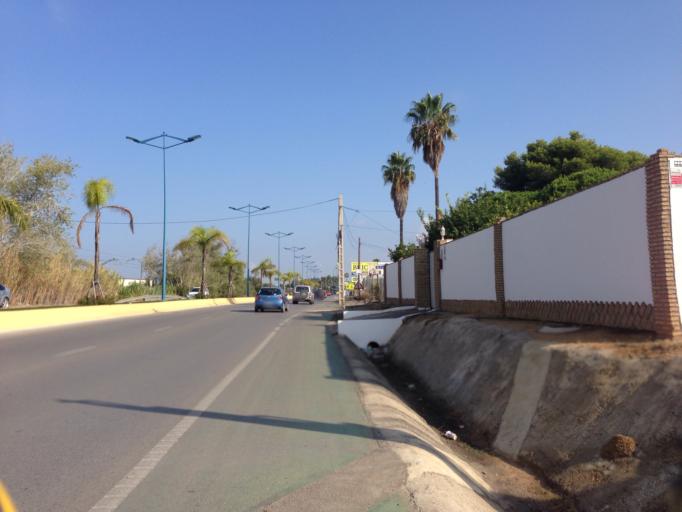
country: ES
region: Andalusia
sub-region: Provincia de Cadiz
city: Chiclana de la Frontera
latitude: 36.4382
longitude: -6.1441
